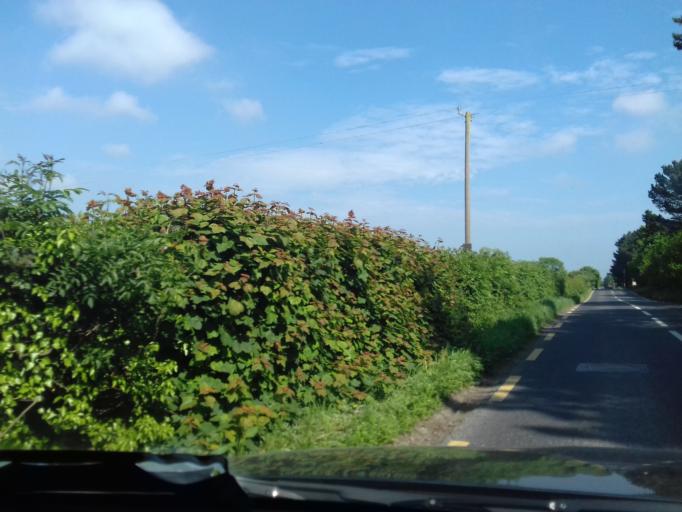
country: IE
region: Leinster
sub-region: Fingal County
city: Swords
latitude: 53.4754
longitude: -6.2673
